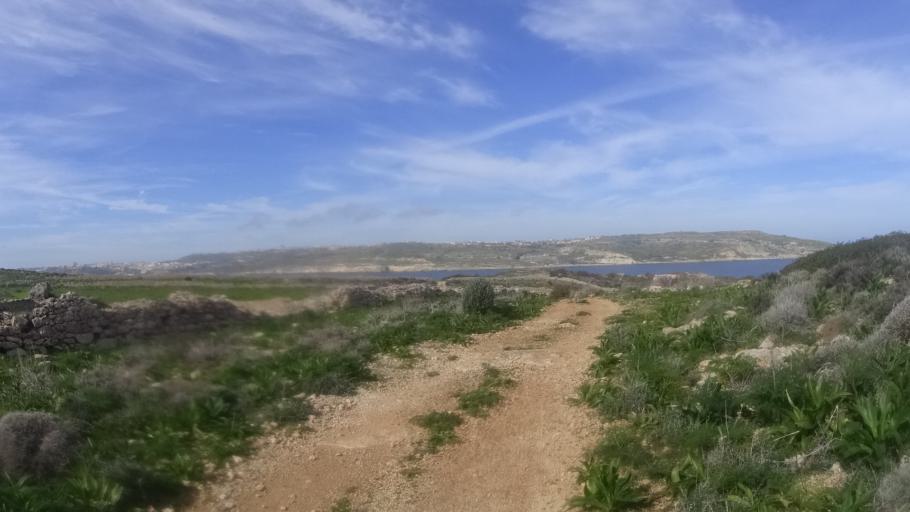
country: MT
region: Il-Qala
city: Qala
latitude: 36.0126
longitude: 14.3293
